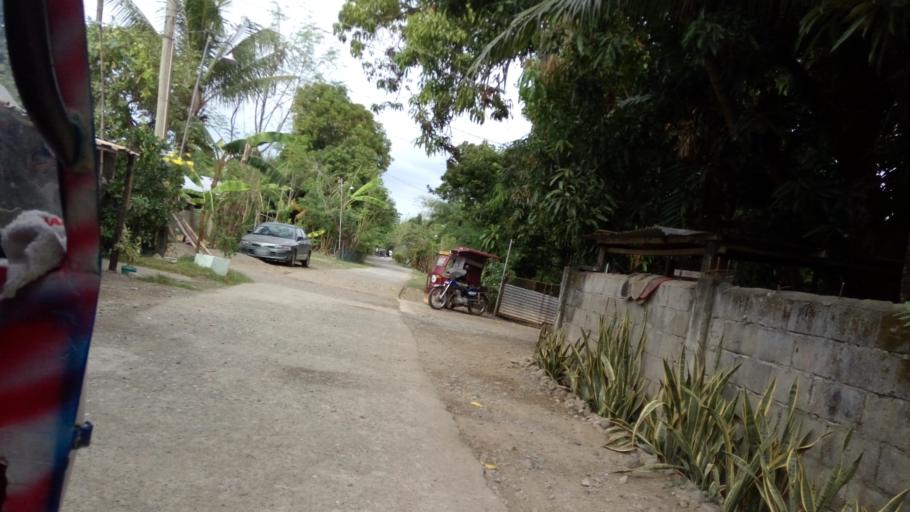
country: PH
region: Ilocos
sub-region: Province of La Union
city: Aringay
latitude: 16.3939
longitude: 120.3520
